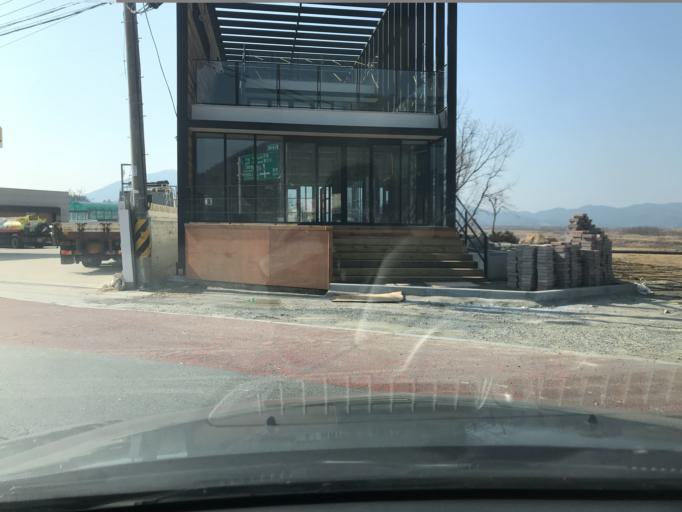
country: KR
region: Daegu
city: Hwawon
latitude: 35.7076
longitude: 128.4368
